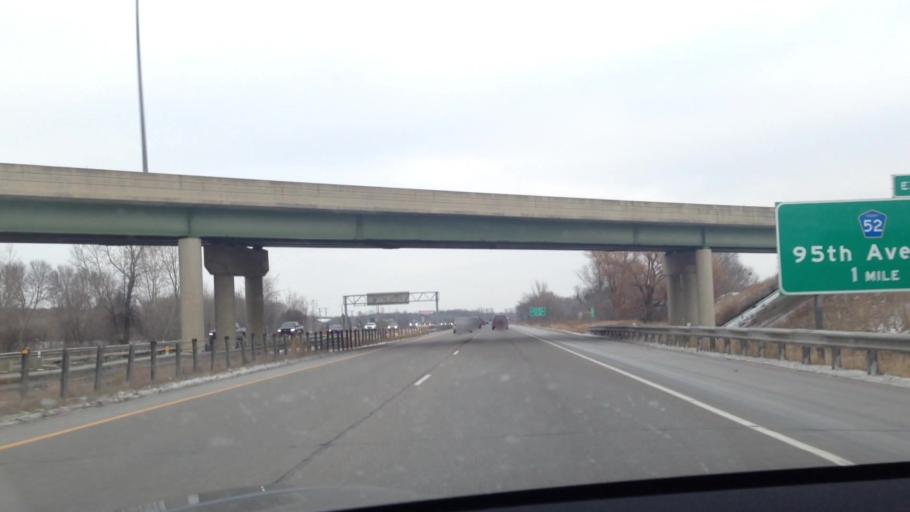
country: US
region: Minnesota
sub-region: Anoka County
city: Lexington
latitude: 45.1279
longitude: -93.1885
